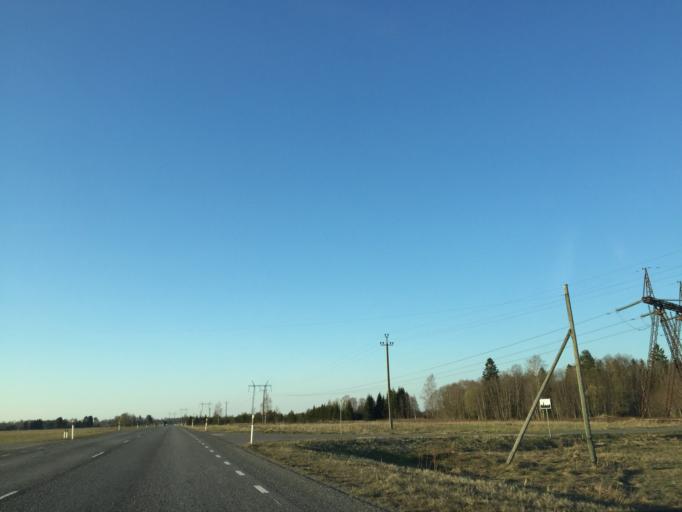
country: EE
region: Ida-Virumaa
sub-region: Johvi vald
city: Johvi
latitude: 59.3035
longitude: 27.4964
